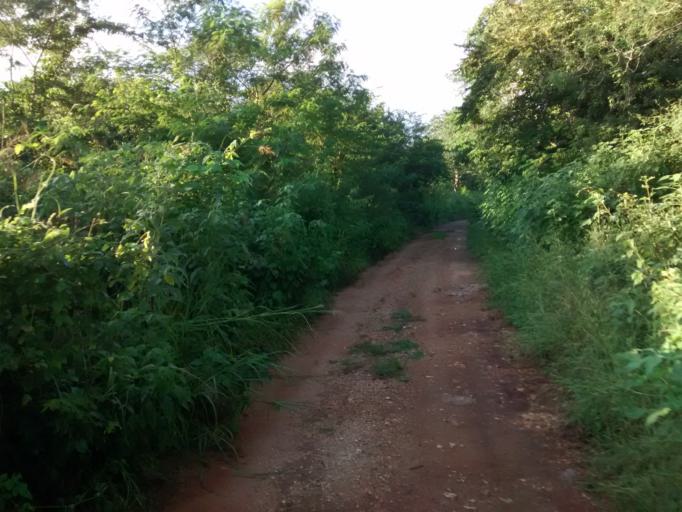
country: MX
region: Yucatan
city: Valladolid
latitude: 20.7073
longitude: -88.2063
